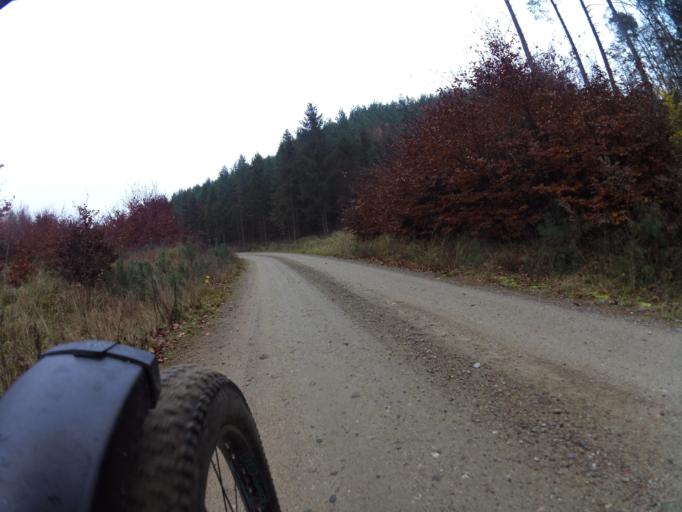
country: PL
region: Pomeranian Voivodeship
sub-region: Powiat wejherowski
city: Orle
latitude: 54.7079
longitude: 18.1466
